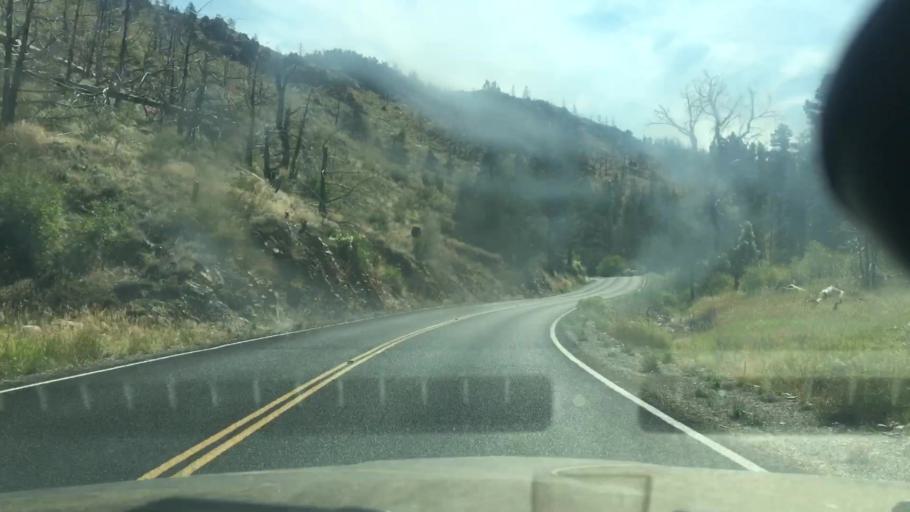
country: US
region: Colorado
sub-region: Larimer County
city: Laporte
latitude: 40.6727
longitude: -105.3866
